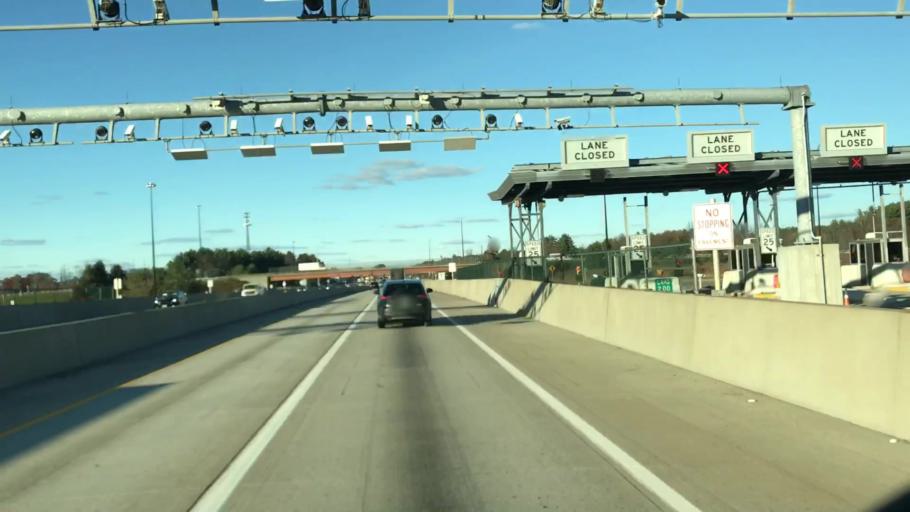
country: US
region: New Hampshire
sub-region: Rockingham County
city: North Hampton
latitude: 42.9623
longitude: -70.8563
